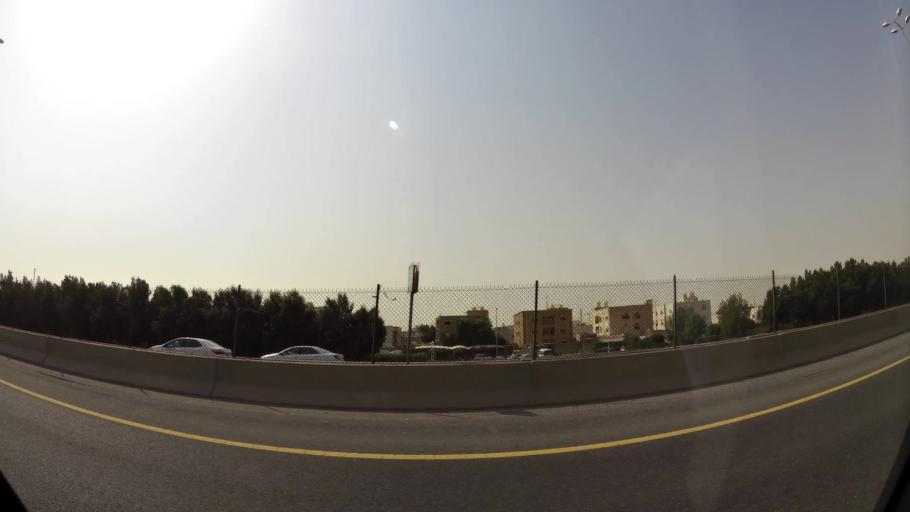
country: KW
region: Muhafazat al Jahra'
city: Al Jahra'
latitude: 29.3493
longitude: 47.6945
